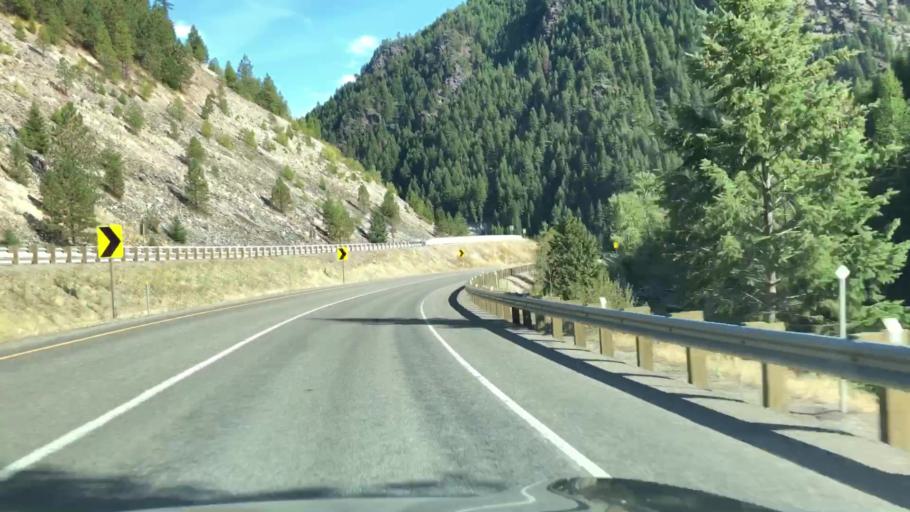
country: US
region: Montana
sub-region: Sanders County
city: Thompson Falls
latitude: 47.3147
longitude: -115.2372
